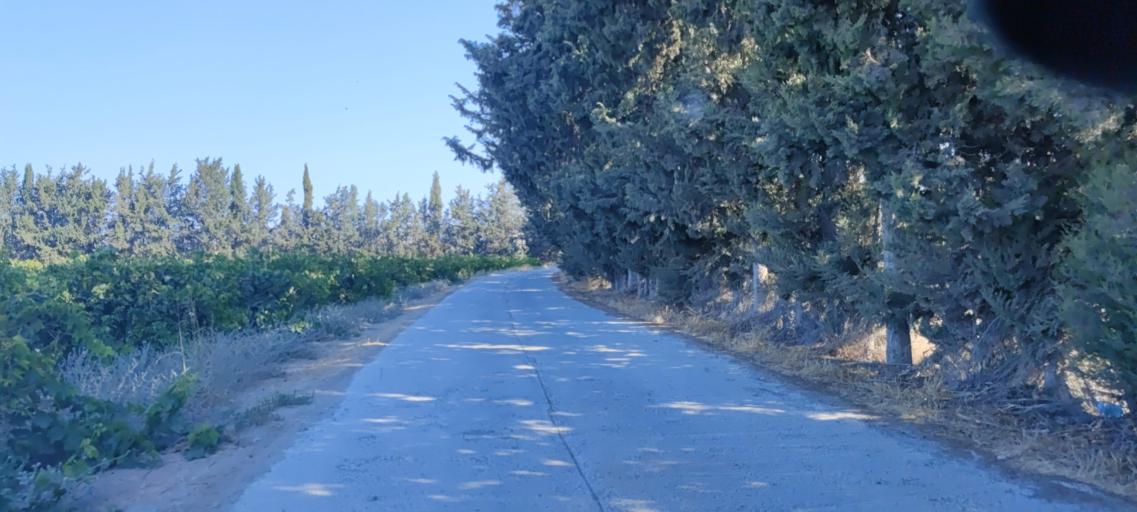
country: CY
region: Limassol
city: Sotira
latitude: 34.6688
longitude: 32.7974
